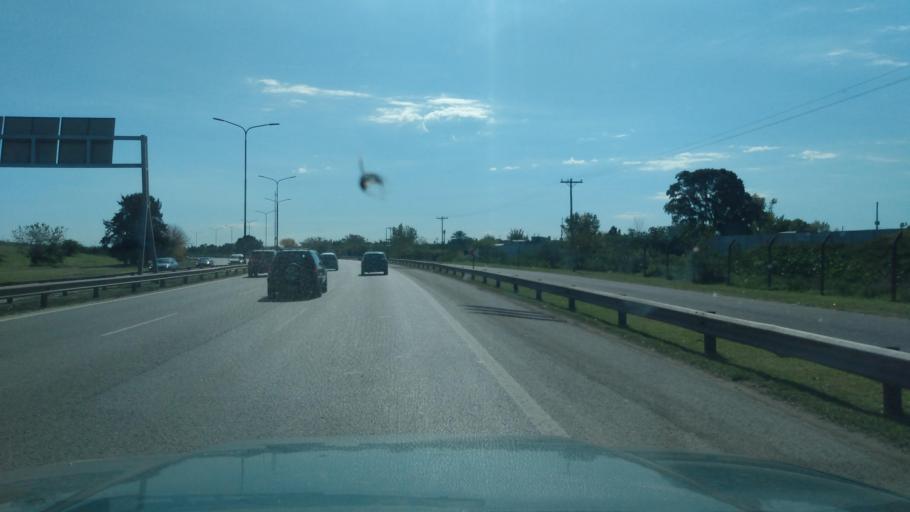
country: AR
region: Buenos Aires
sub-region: Partido de Tigre
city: Tigre
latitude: -34.5015
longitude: -58.5894
